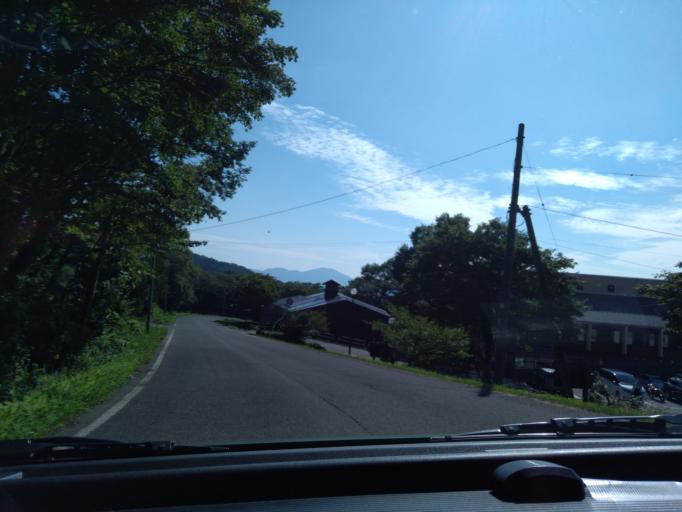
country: JP
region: Iwate
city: Shizukuishi
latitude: 39.7646
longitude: 140.7539
